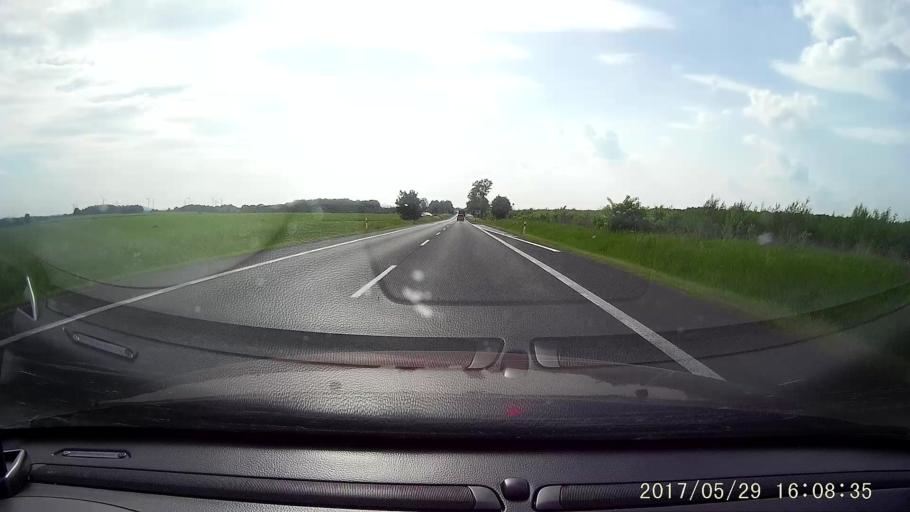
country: PL
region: Lower Silesian Voivodeship
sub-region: Powiat zgorzelecki
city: Piensk
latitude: 51.2039
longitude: 15.1307
